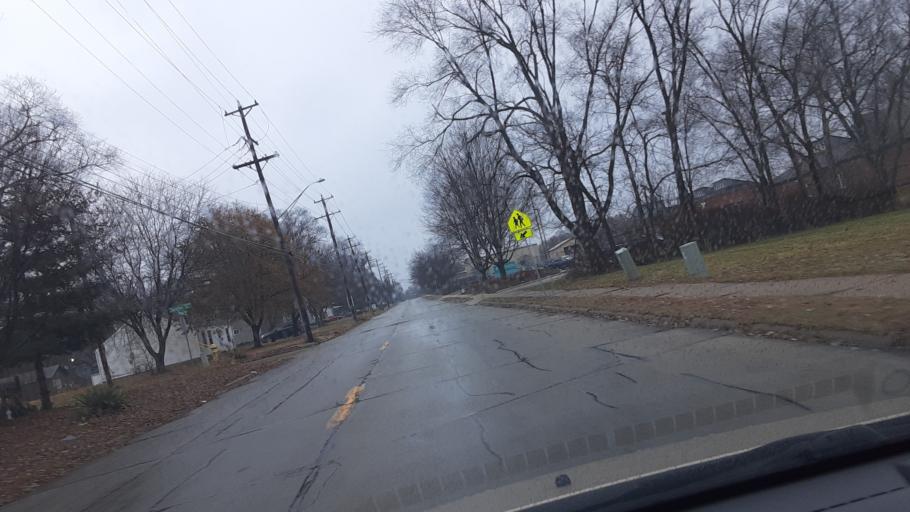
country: US
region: Illinois
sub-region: Winnebago County
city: Rockford
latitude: 42.3011
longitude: -89.1046
